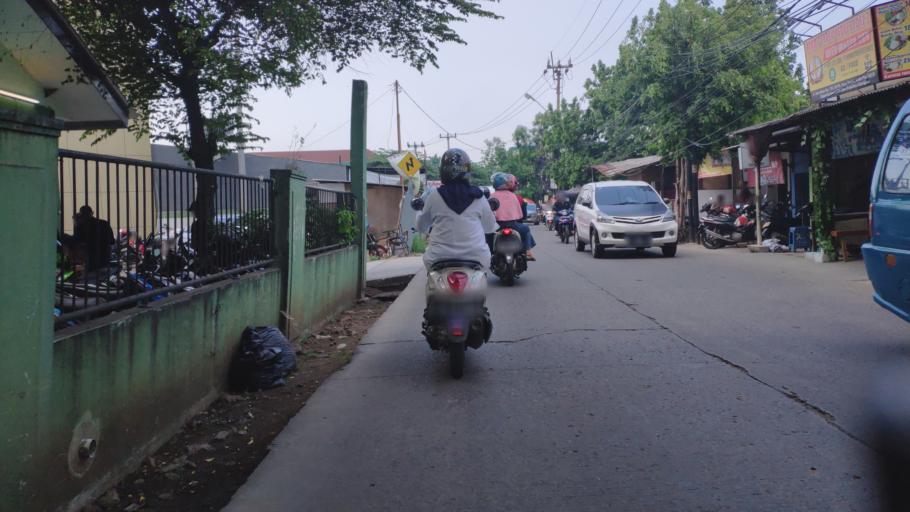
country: ID
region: West Java
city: Pamulang
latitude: -6.3551
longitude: 106.7754
